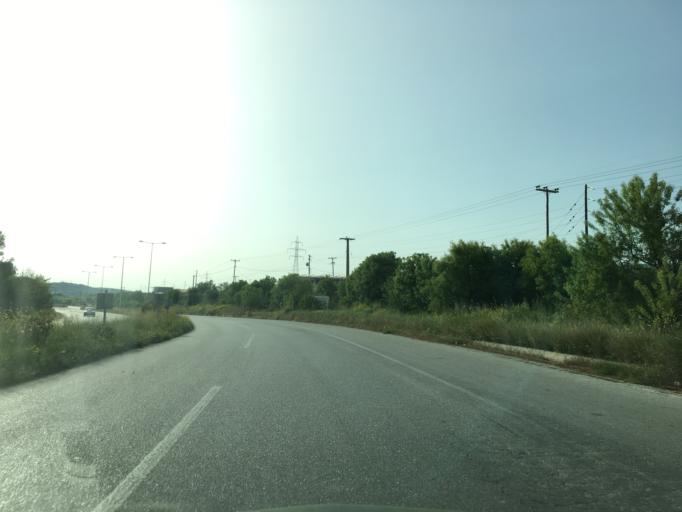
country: GR
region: Thessaly
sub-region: Nomos Magnisias
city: Nea Ionia
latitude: 39.3843
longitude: 22.8491
